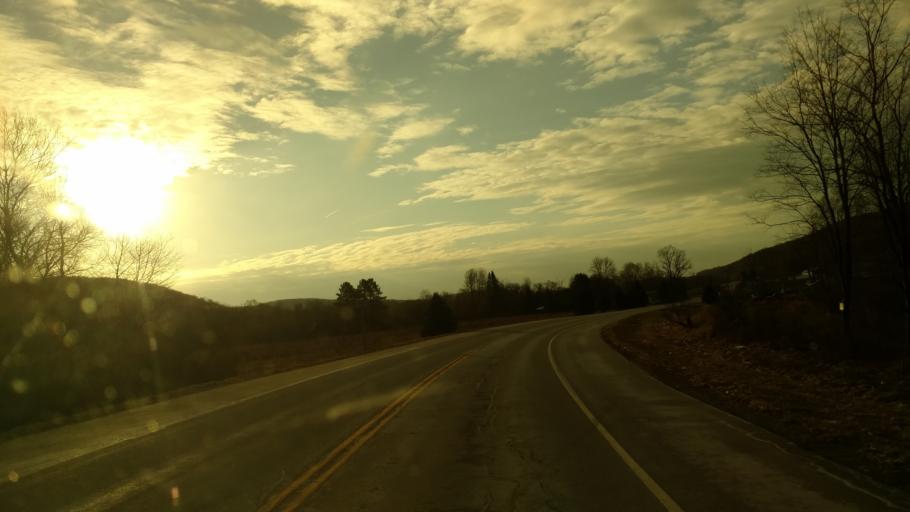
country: US
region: New York
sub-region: Allegany County
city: Wellsville
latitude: 42.0136
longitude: -77.8924
